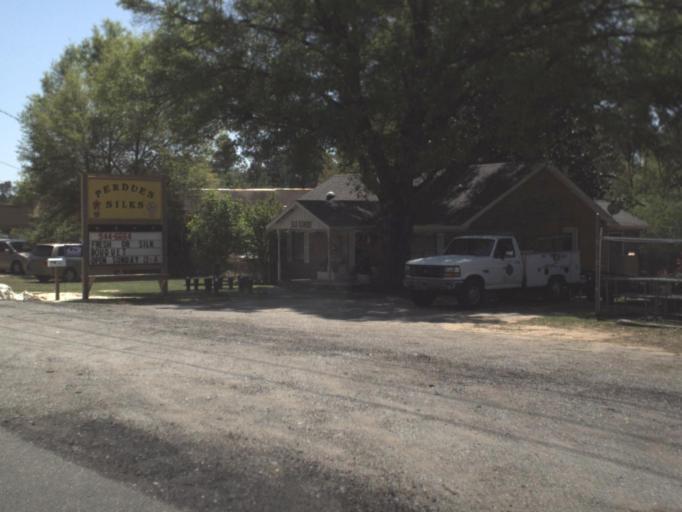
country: US
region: Florida
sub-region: Escambia County
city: Ensley
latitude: 30.5122
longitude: -87.3097
